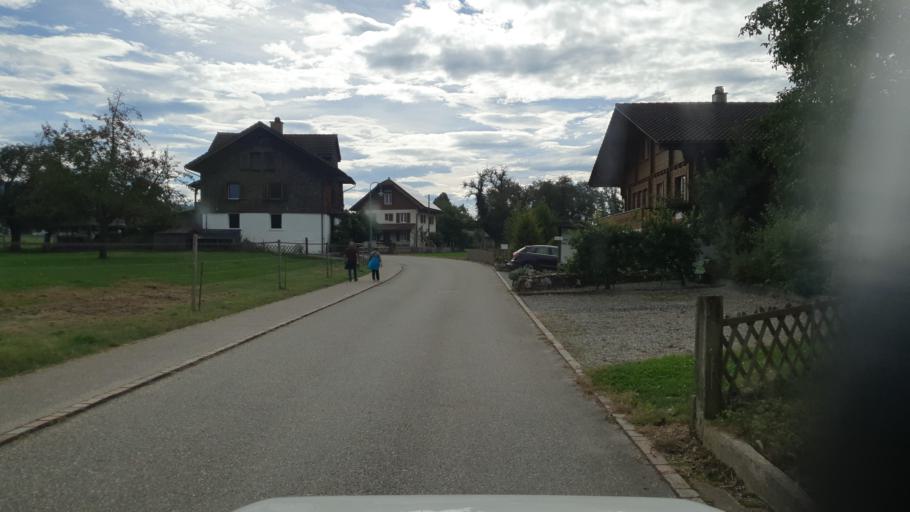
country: CH
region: Aargau
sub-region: Bezirk Lenzburg
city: Meisterschwanden
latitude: 47.2575
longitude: 8.2352
